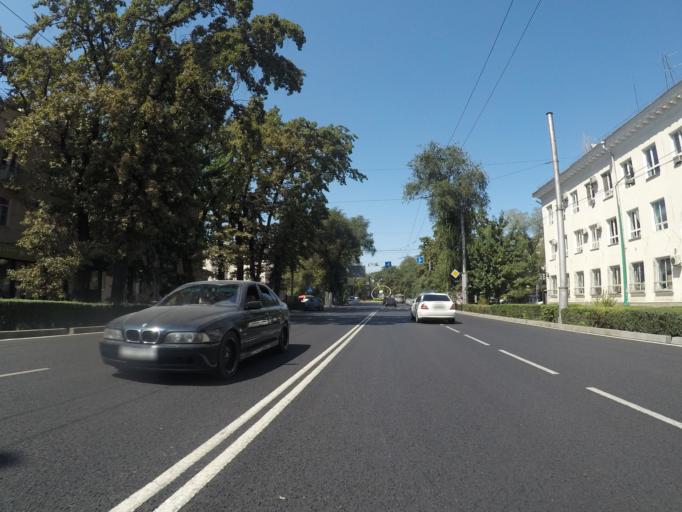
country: KG
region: Chuy
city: Bishkek
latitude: 42.8769
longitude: 74.5822
